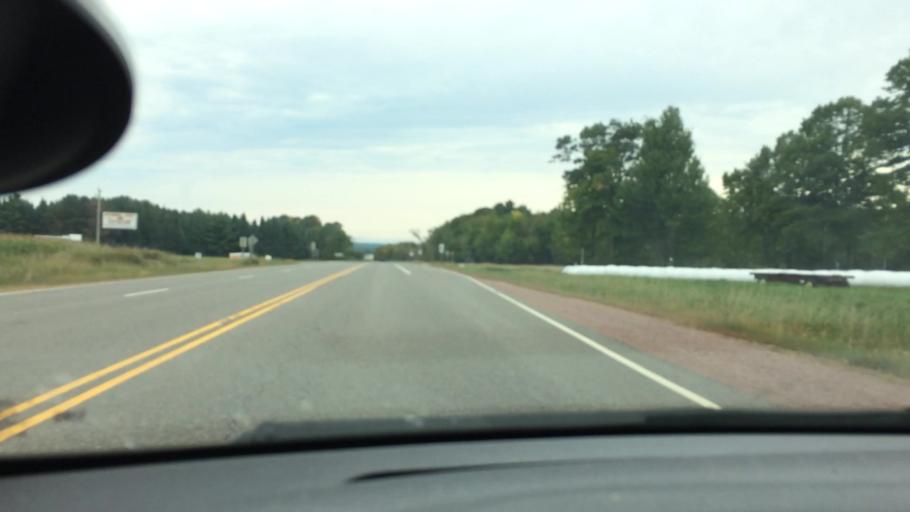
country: US
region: Wisconsin
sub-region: Clark County
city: Neillsville
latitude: 44.5643
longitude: -90.6578
